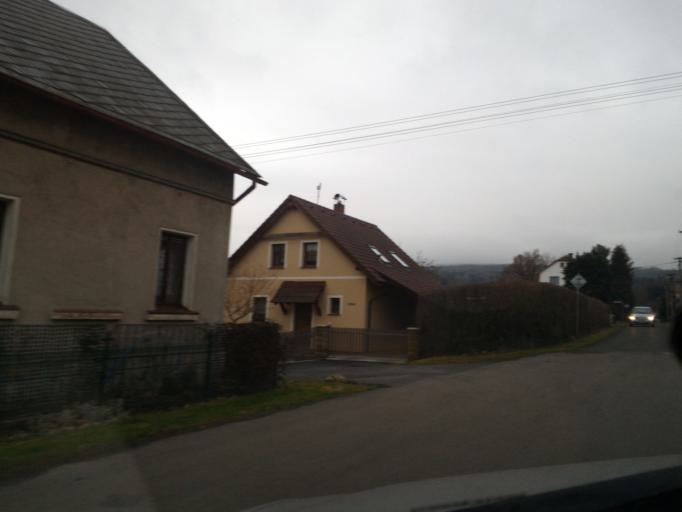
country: CZ
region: Ustecky
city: Varnsdorf
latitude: 50.9080
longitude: 14.6065
